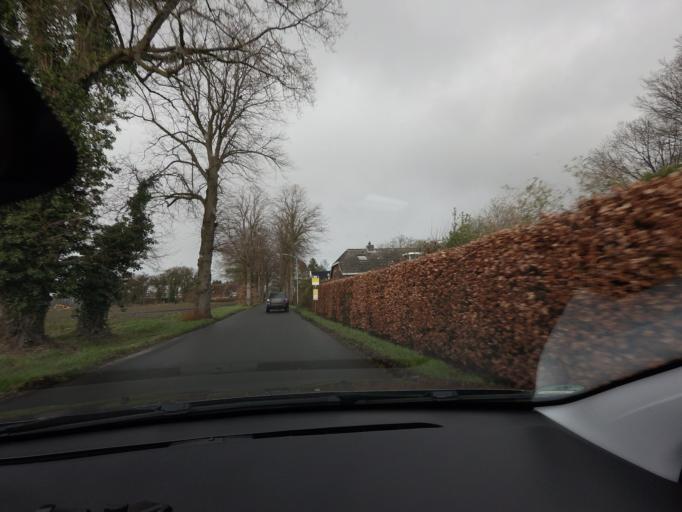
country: NL
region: Drenthe
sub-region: Gemeente Aa en Hunze
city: Anloo
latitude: 53.0111
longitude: 6.7697
